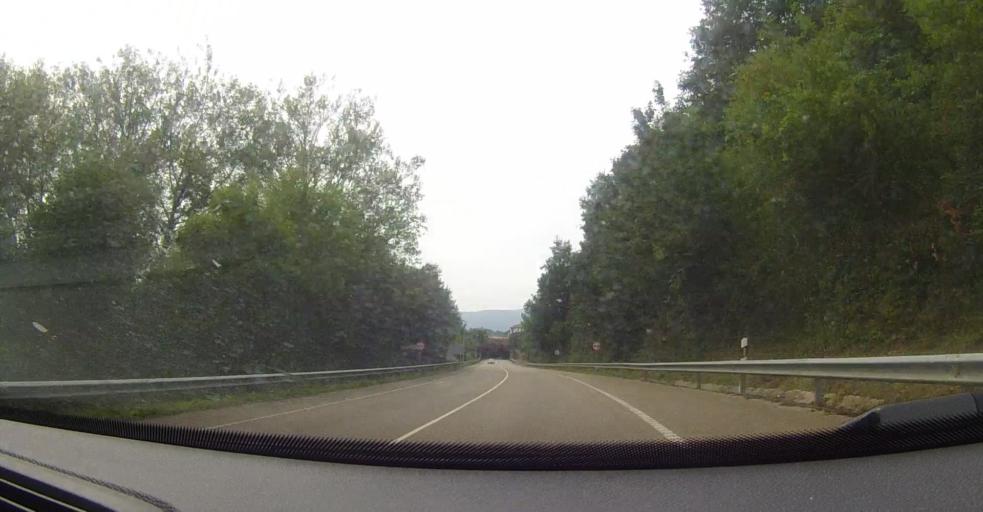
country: ES
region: Asturias
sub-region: Province of Asturias
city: Cangas de Onis
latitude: 43.3549
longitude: -5.1260
